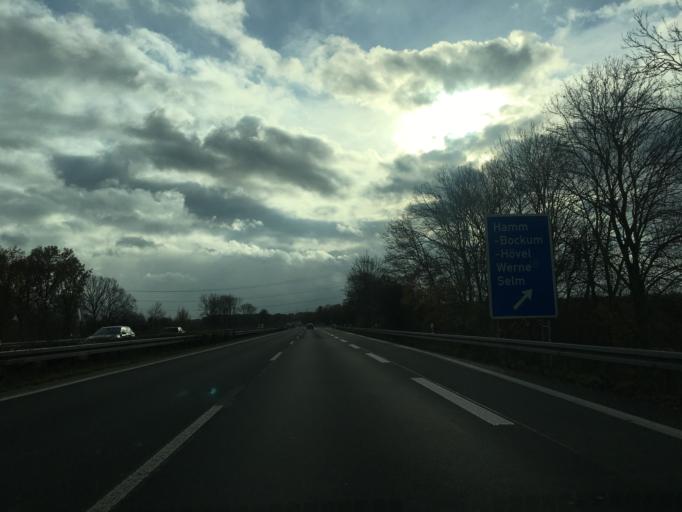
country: DE
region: North Rhine-Westphalia
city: Werne
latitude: 51.6975
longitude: 7.6663
